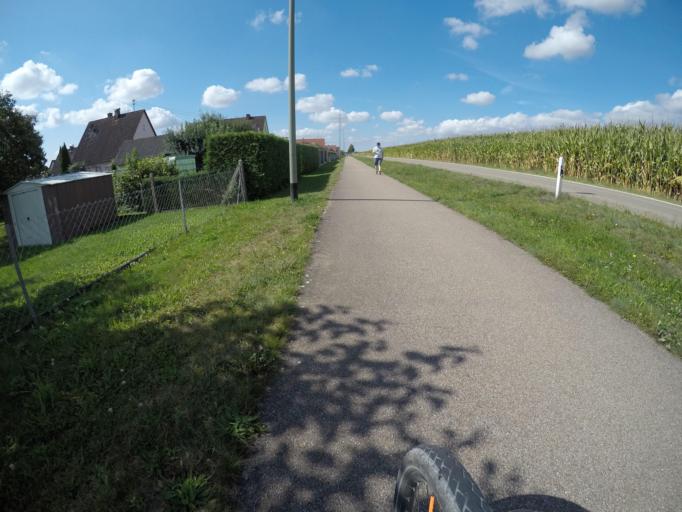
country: DE
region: Bavaria
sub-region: Swabia
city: Hochstadt an der Donau
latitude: 48.6208
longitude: 10.5583
